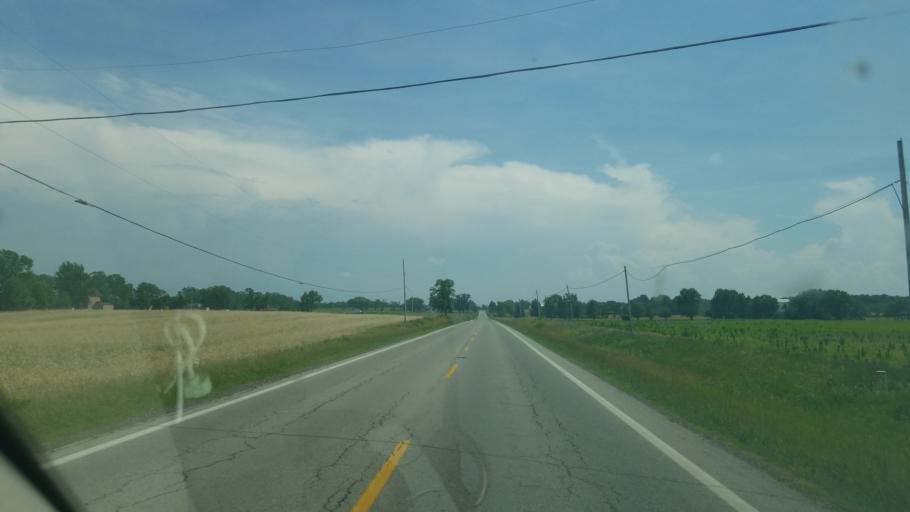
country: US
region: Ohio
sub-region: Logan County
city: Northwood
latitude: 40.4949
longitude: -83.7422
